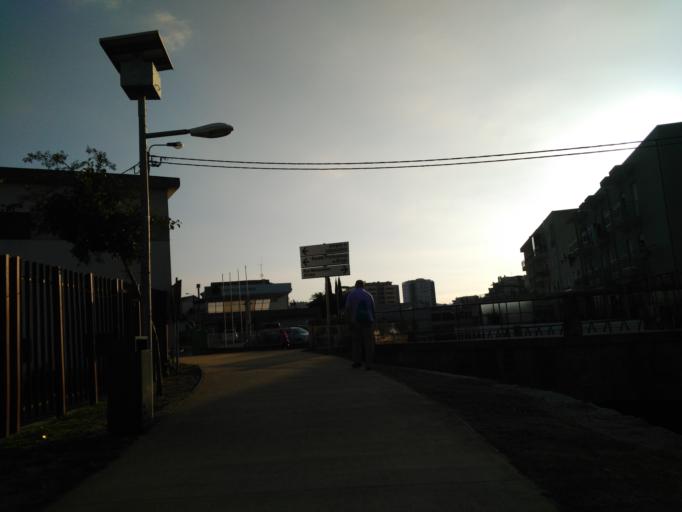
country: PT
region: Braga
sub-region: Braga
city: Braga
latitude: 41.5415
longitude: -8.4250
